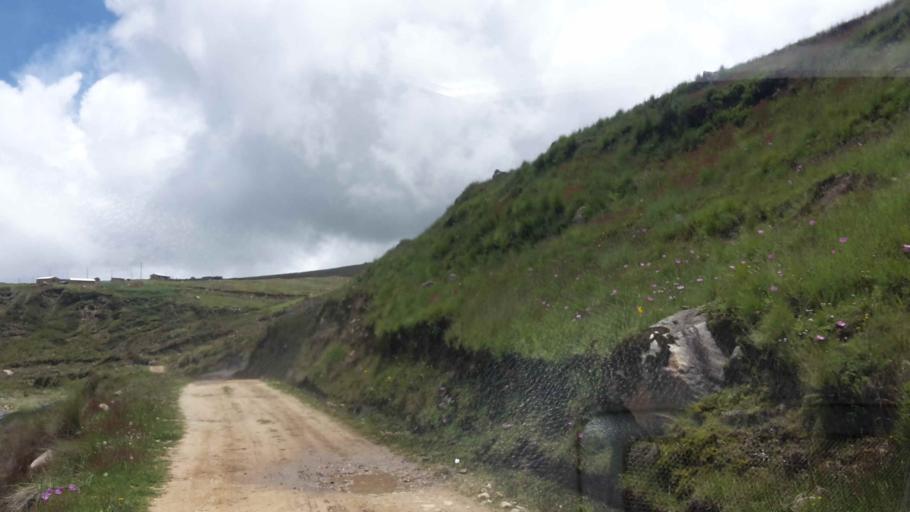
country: BO
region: Cochabamba
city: Cochabamba
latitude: -17.1840
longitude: -66.0639
